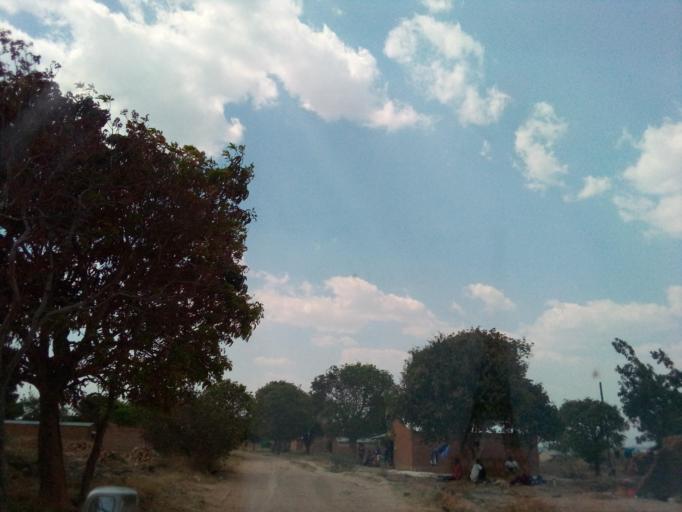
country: ZM
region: Northern
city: Mpika
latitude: -11.8347
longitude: 31.3878
